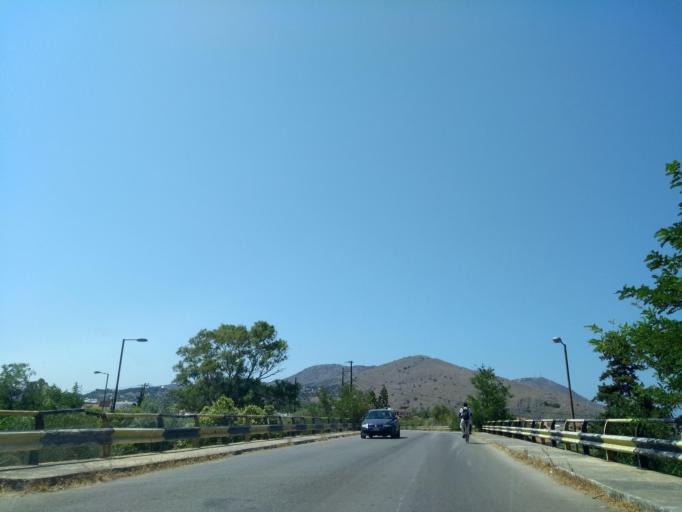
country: GR
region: Crete
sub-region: Nomos Chanias
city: Georgioupolis
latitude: 35.3574
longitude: 24.2635
